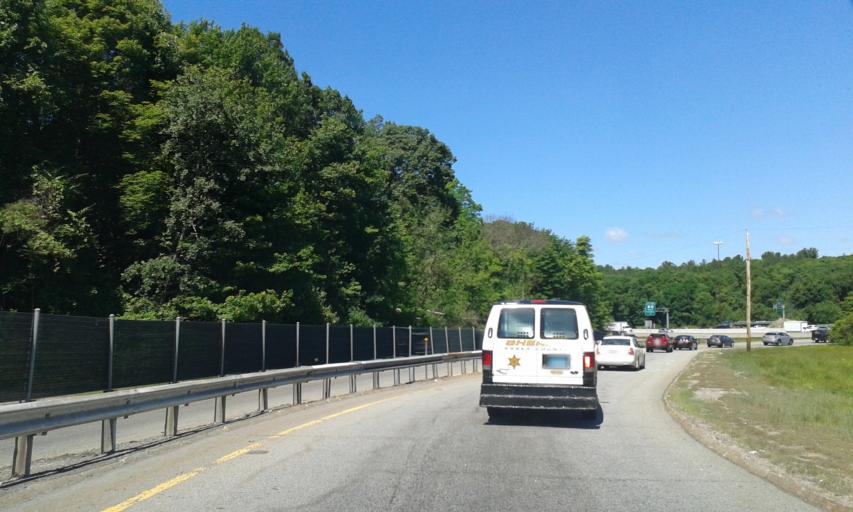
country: US
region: Massachusetts
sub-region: Middlesex County
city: Lexington
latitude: 42.4744
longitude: -71.2201
